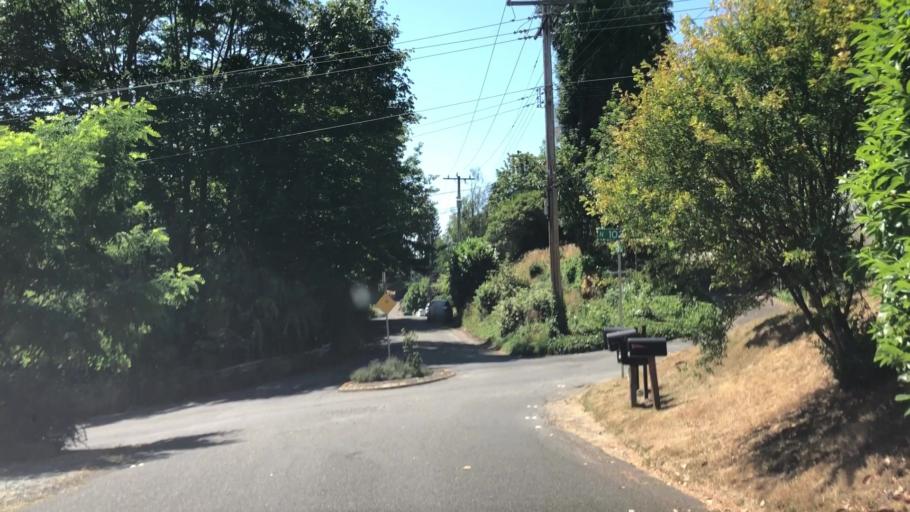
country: US
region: Washington
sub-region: King County
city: Shoreline
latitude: 47.7035
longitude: -122.3376
